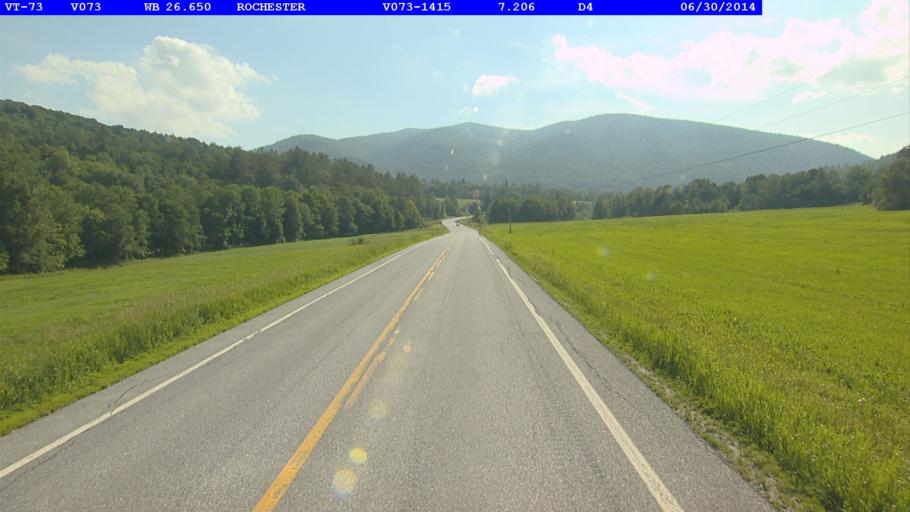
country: US
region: Vermont
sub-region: Orange County
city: Randolph
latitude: 43.8512
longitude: -72.8336
